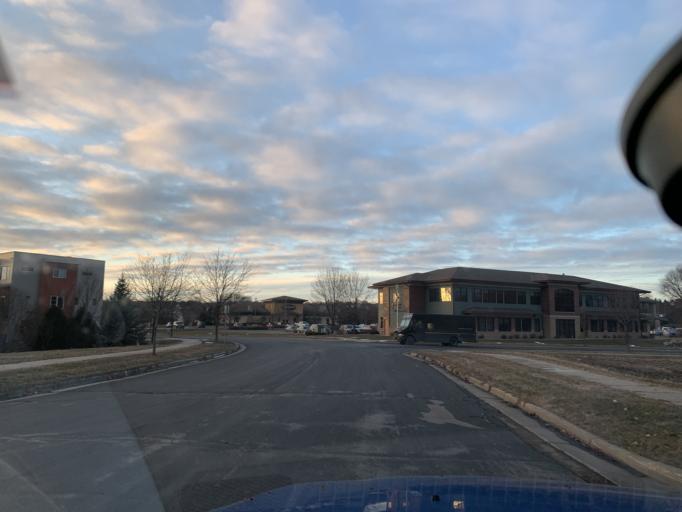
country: US
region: Wisconsin
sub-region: Dane County
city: Madison
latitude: 43.0141
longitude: -89.4281
